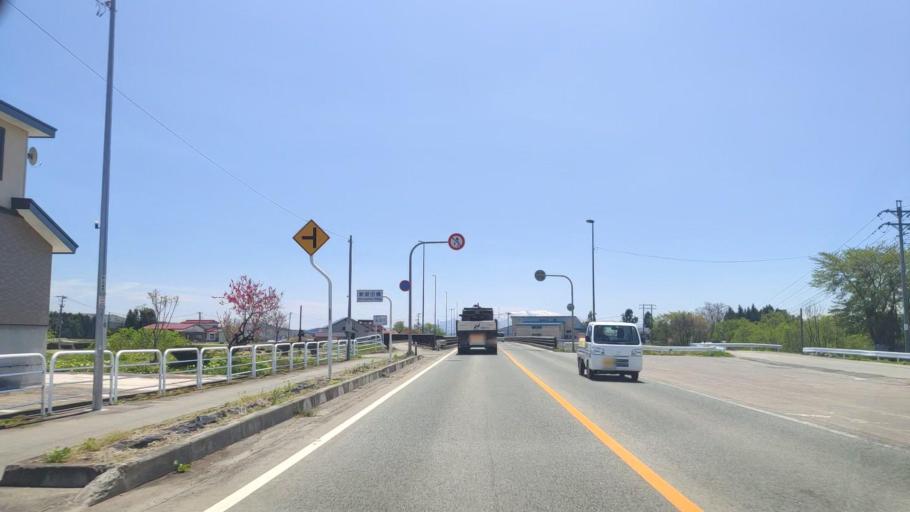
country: JP
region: Yamagata
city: Shinjo
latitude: 38.7990
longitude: 140.3193
